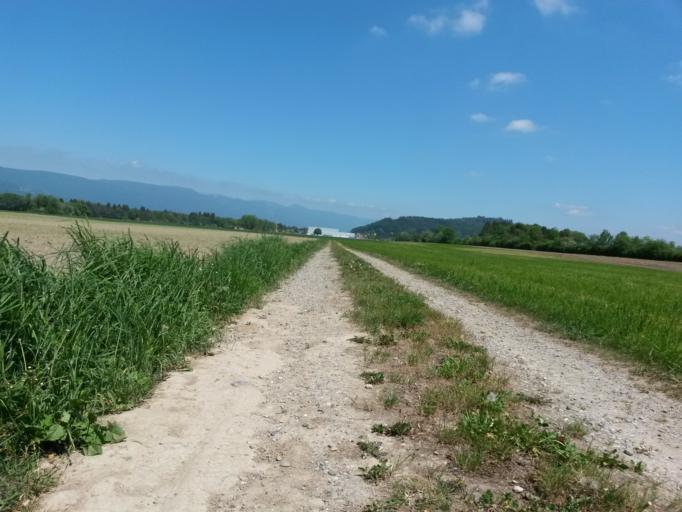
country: CH
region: Bern
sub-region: Seeland District
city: Worben
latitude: 47.1055
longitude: 7.3220
